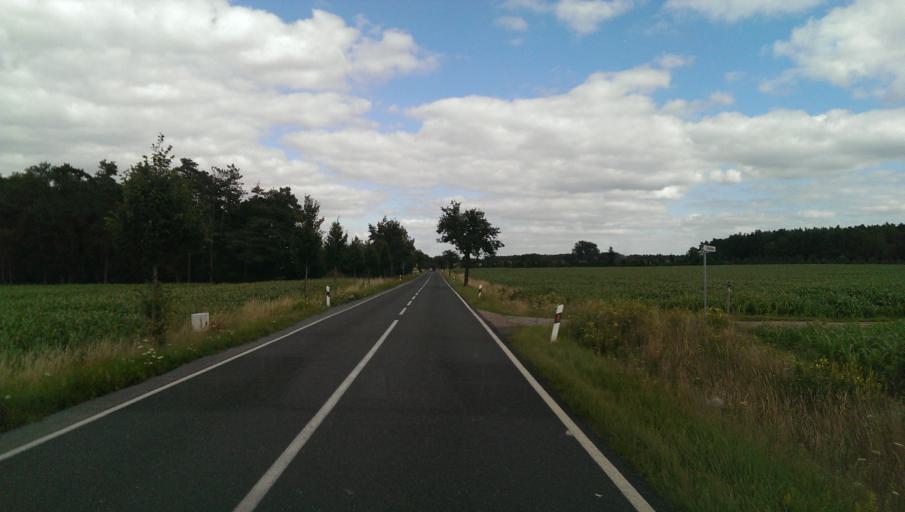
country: DE
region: Saxony-Anhalt
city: Radis
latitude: 51.7864
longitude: 12.4769
